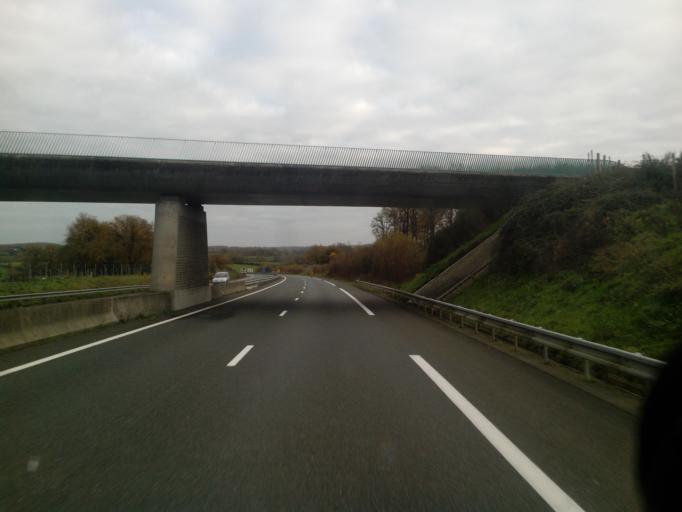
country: FR
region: Poitou-Charentes
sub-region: Departement des Deux-Sevres
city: Le Pin
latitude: 46.9009
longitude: -0.6641
